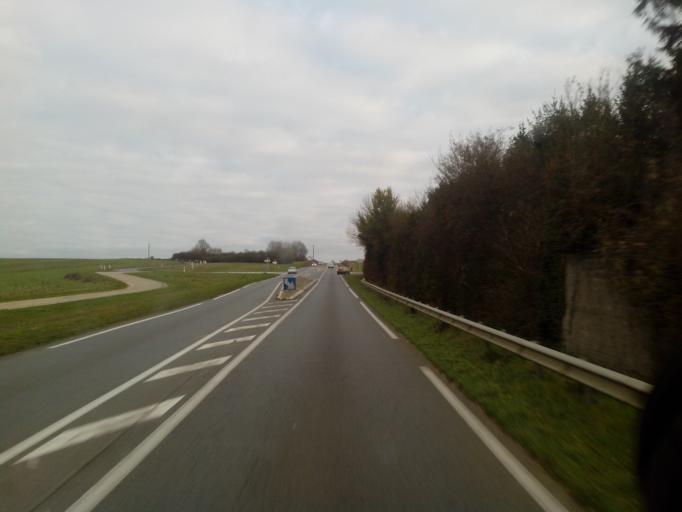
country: FR
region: Poitou-Charentes
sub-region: Departement de la Vienne
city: Cisse
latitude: 46.6410
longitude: 0.2022
